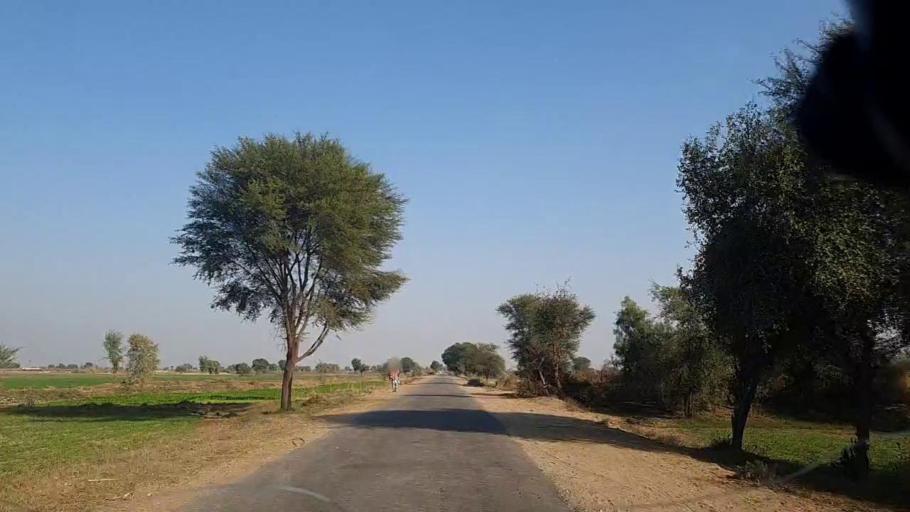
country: PK
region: Sindh
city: Khanpur
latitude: 27.6882
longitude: 69.5014
